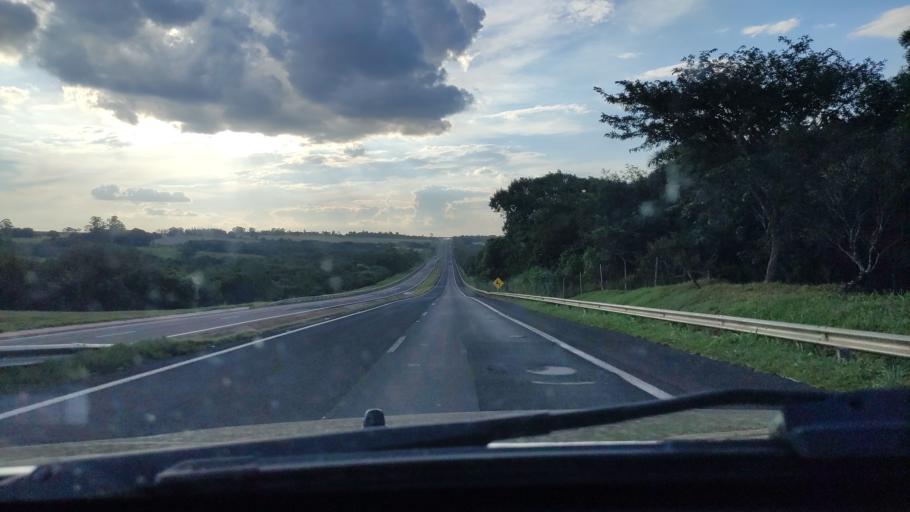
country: BR
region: Sao Paulo
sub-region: Rancharia
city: Rancharia
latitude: -22.4919
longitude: -50.9108
